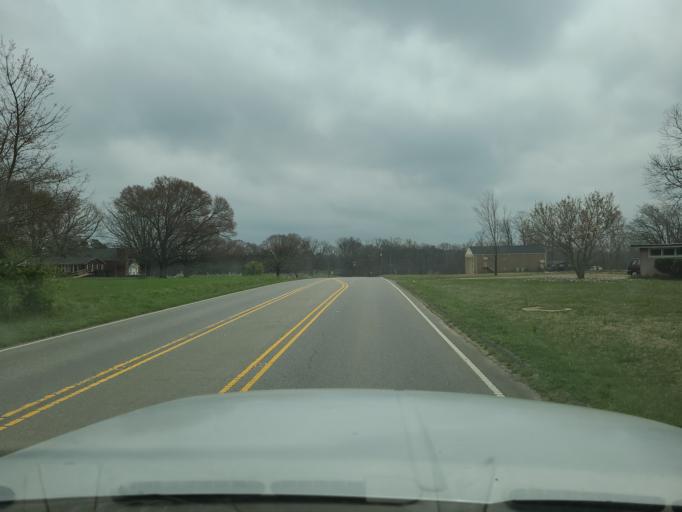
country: US
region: North Carolina
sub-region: Cleveland County
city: Shelby
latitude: 35.3888
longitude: -81.6235
